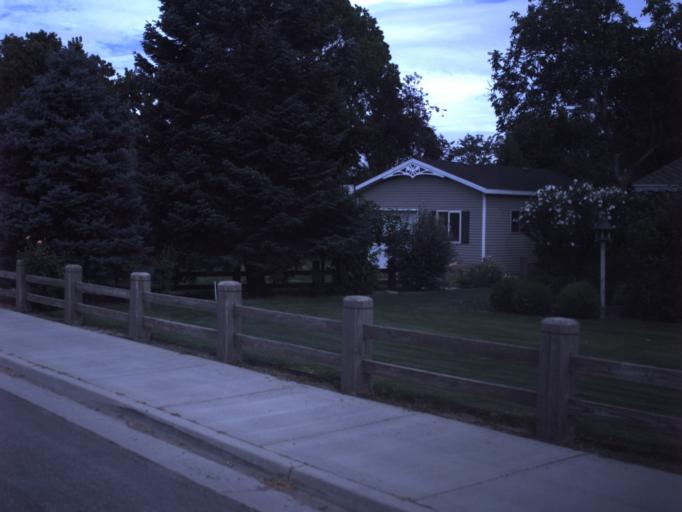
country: US
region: Utah
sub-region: Davis County
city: South Weber
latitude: 41.1347
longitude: -111.9563
